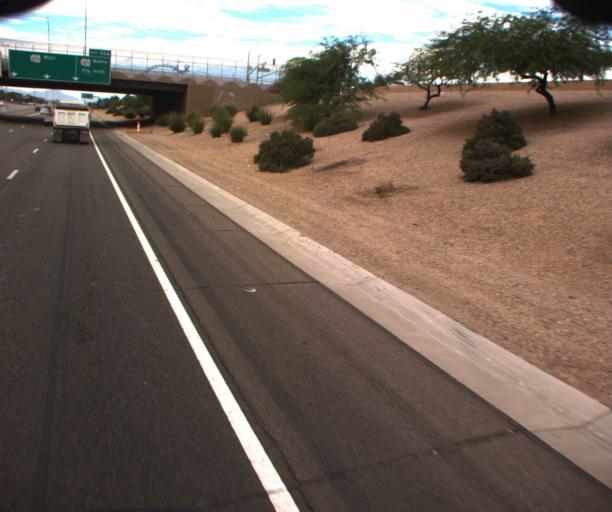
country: US
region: Arizona
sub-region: Maricopa County
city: Chandler
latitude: 33.2874
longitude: -111.8577
